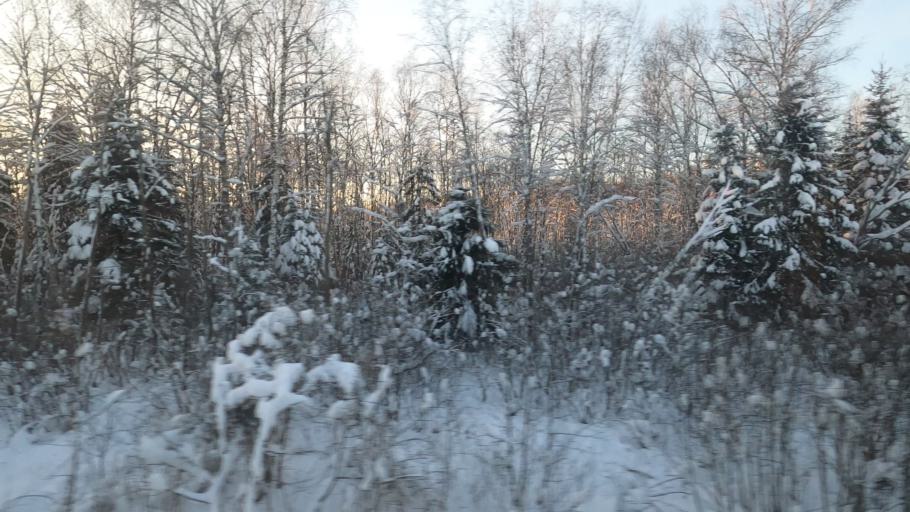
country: RU
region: Moskovskaya
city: Novo-Nikol'skoye
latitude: 56.5647
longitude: 37.5663
